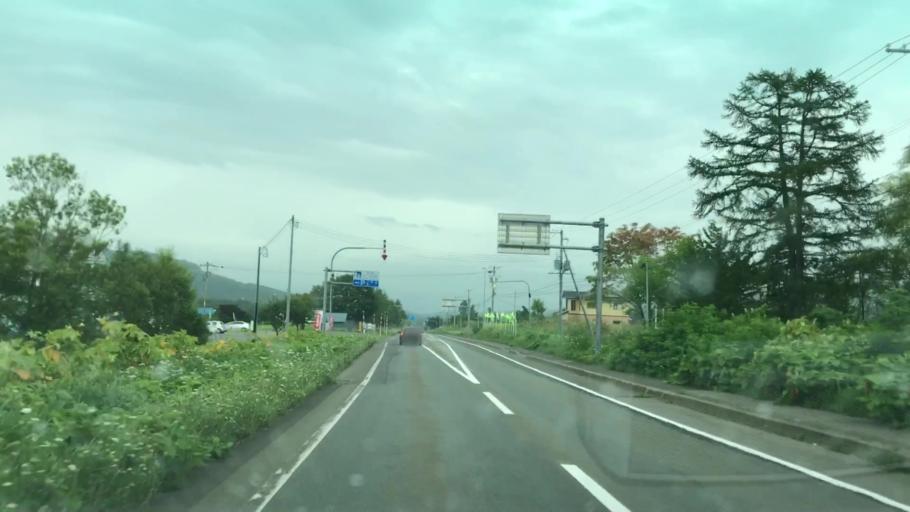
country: JP
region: Hokkaido
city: Niseko Town
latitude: 42.7612
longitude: 140.4789
